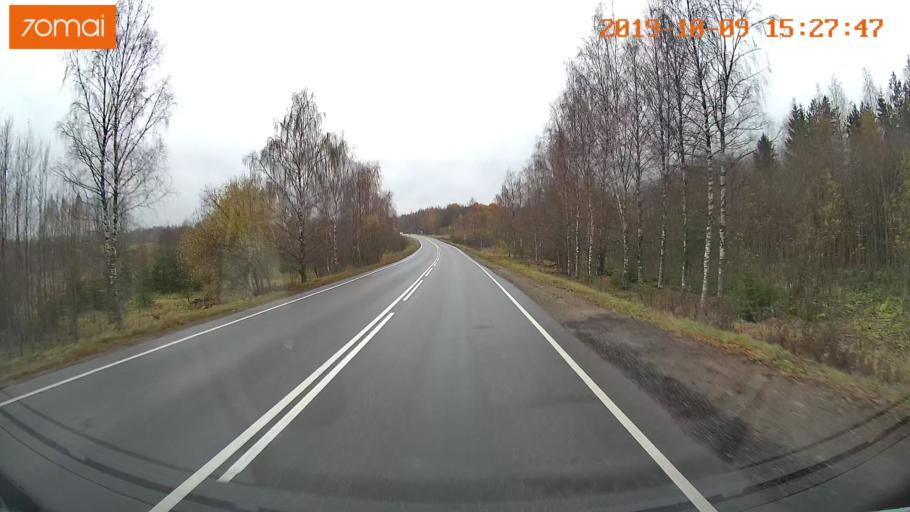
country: RU
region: Kostroma
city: Susanino
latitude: 58.0104
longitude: 41.3715
